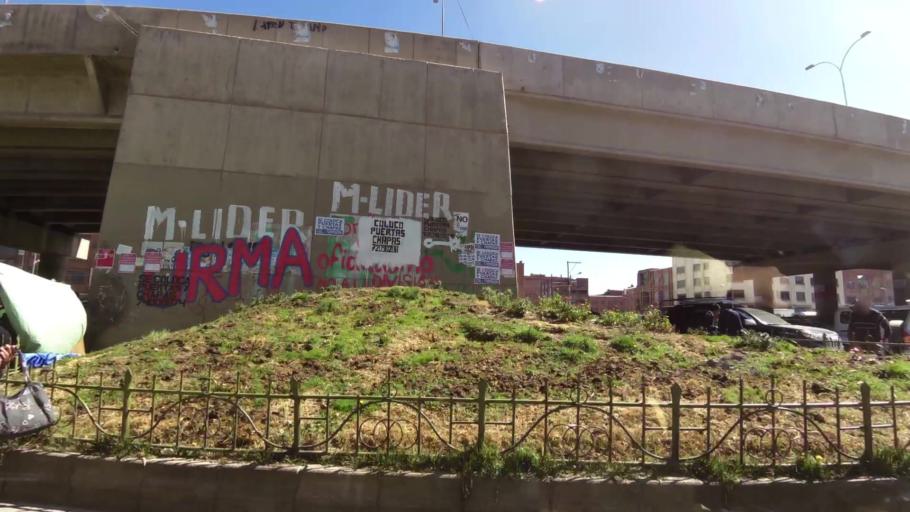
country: BO
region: La Paz
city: La Paz
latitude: -16.5350
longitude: -68.1907
